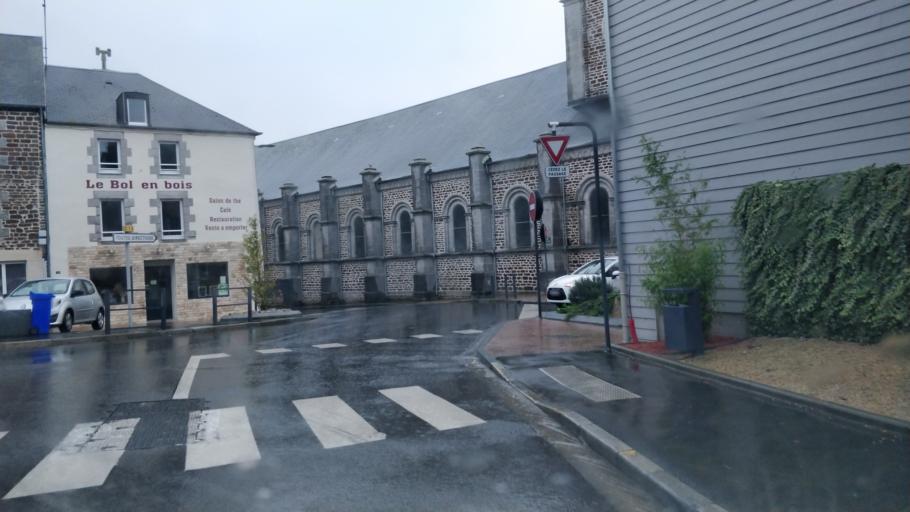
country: FR
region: Lower Normandy
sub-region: Departement de la Manche
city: Brehal
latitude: 48.8997
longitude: -1.5128
